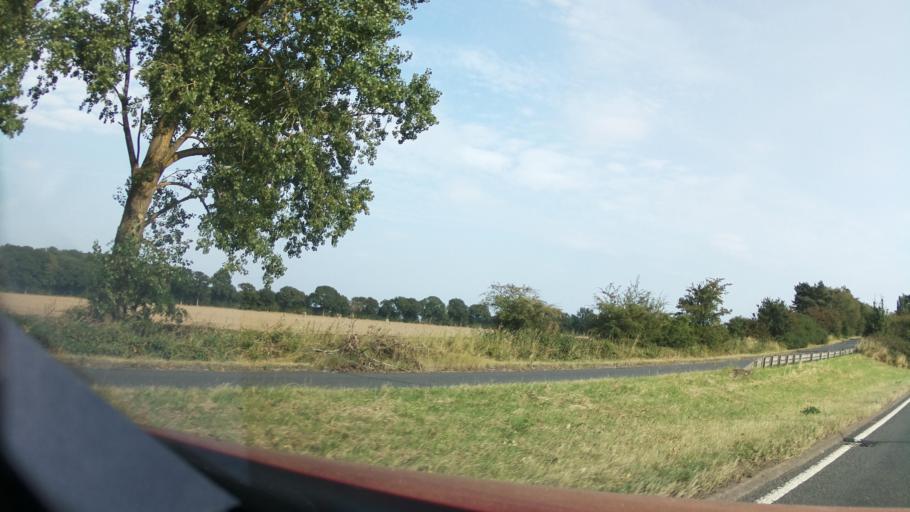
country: GB
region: England
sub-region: Solihull
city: Tidbury Green
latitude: 52.3478
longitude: -1.8790
